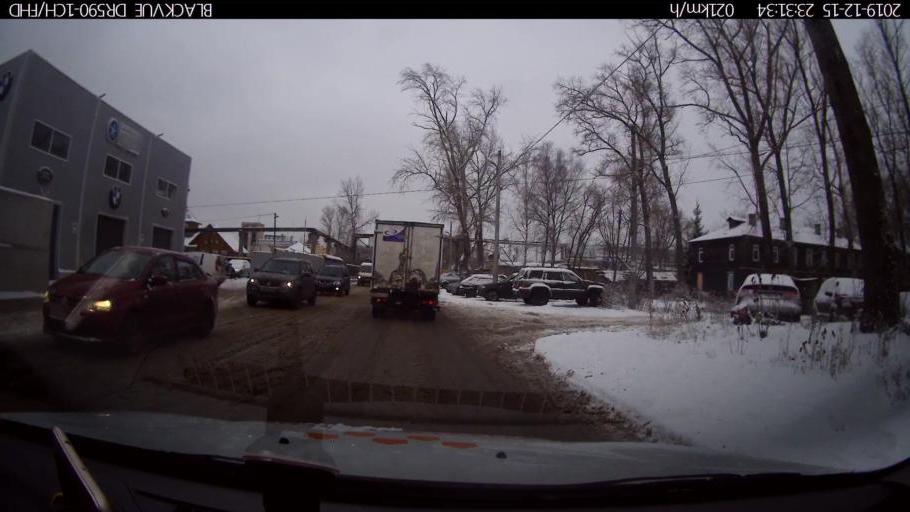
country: RU
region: Nizjnij Novgorod
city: Nizhniy Novgorod
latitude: 56.3155
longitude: 43.9123
